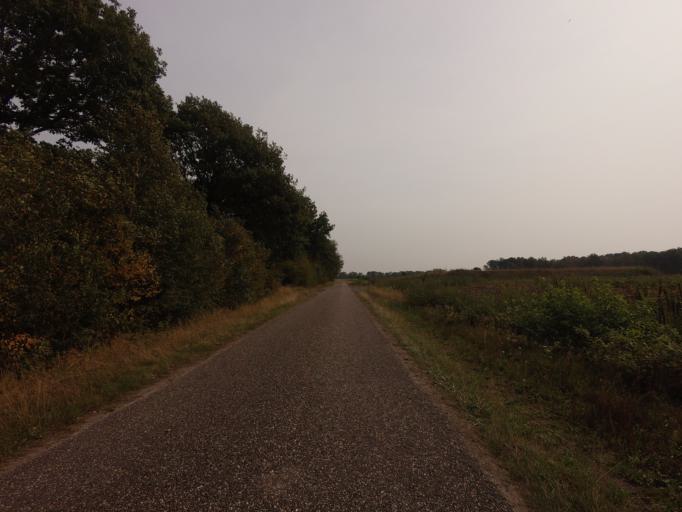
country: NL
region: Drenthe
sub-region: Gemeente Tynaarlo
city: Vries
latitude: 53.1088
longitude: 6.5450
